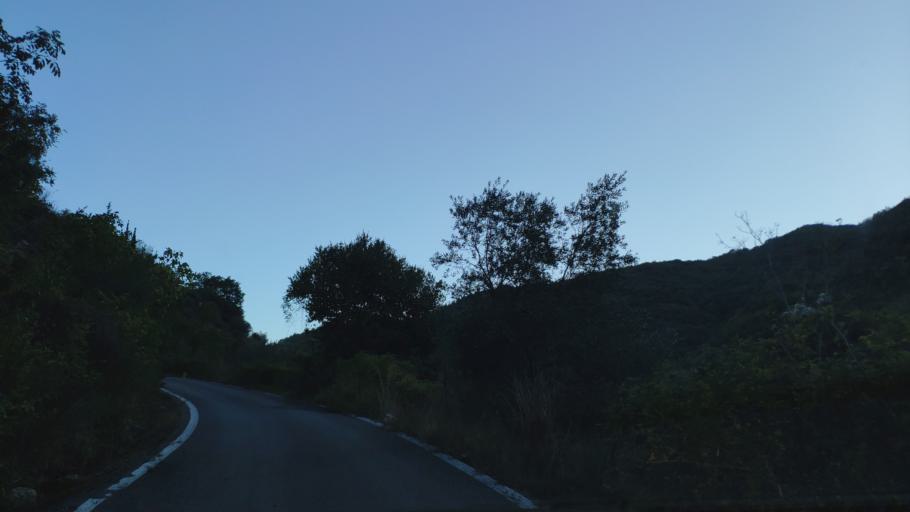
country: GR
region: Peloponnese
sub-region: Nomos Arkadias
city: Dimitsana
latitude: 37.5714
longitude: 22.0443
